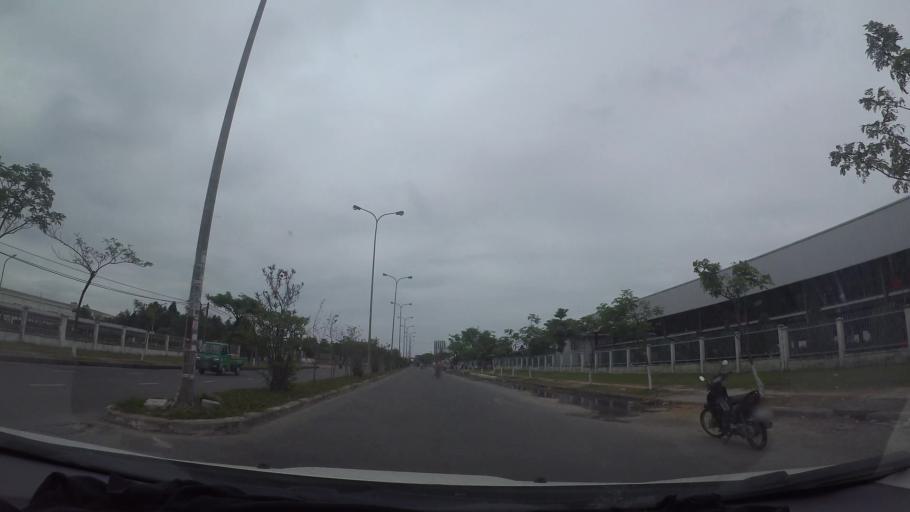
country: VN
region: Da Nang
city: Lien Chieu
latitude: 16.0758
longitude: 108.1386
